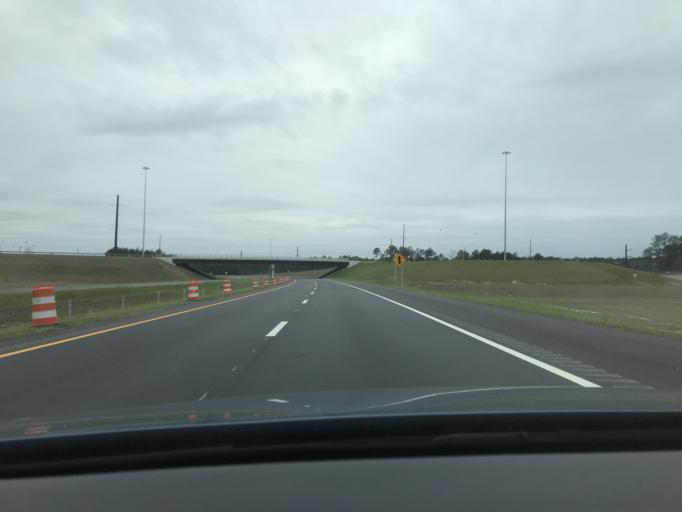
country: US
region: North Carolina
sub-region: Cumberland County
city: Fort Bragg
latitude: 35.1073
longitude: -79.0104
